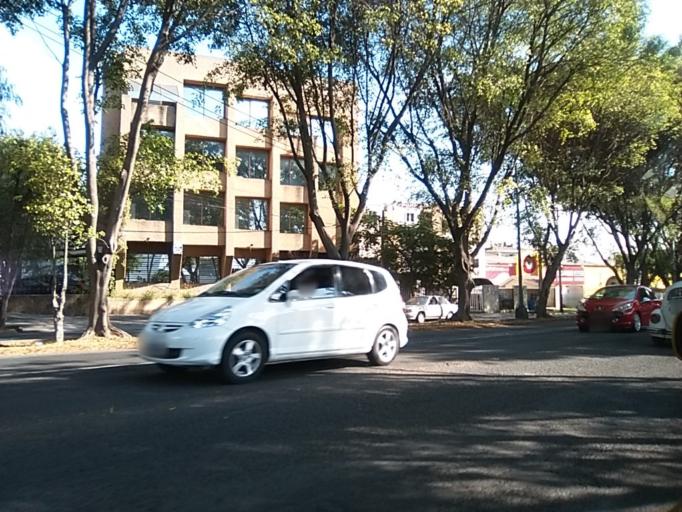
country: MX
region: Jalisco
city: Guadalajara
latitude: 20.6624
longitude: -103.3786
